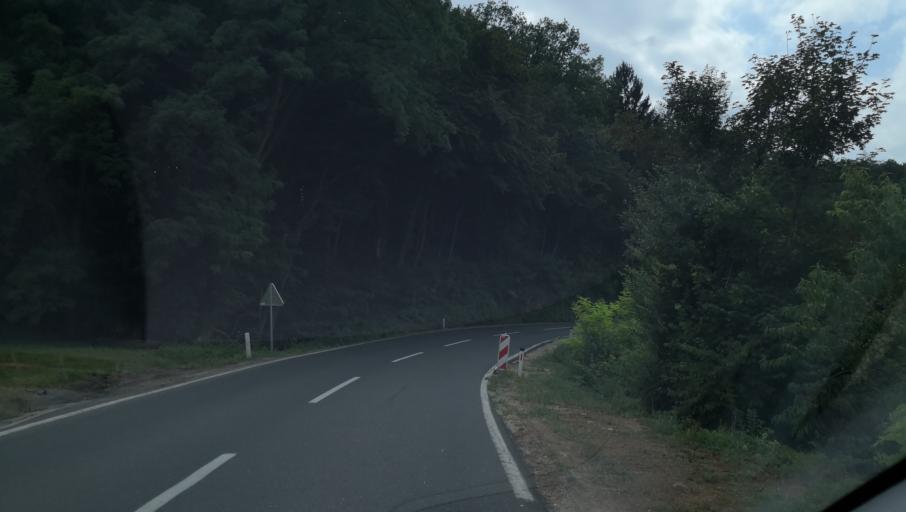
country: SI
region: Novo Mesto
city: Novo Mesto
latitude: 45.7720
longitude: 15.1898
